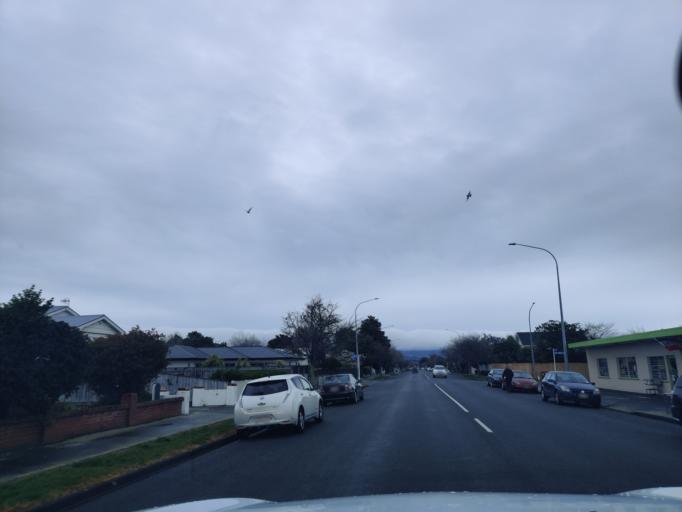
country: NZ
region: Manawatu-Wanganui
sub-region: Palmerston North City
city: Palmerston North
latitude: -40.3419
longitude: 175.6142
